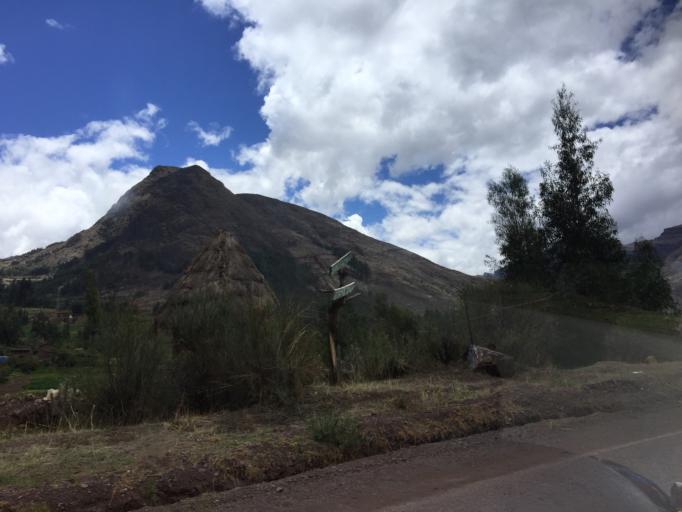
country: PE
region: Cusco
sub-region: Provincia de Calca
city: Pisac
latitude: -13.4067
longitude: -71.8316
